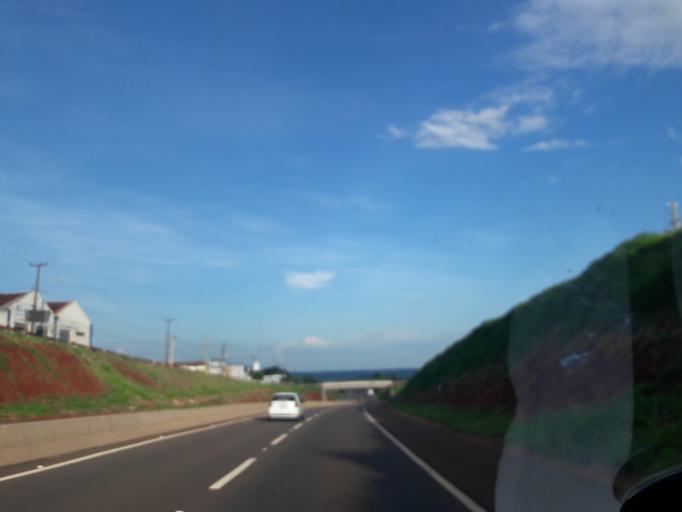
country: BR
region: Parana
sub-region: Engenheiro Beltrao
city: Engenheiro Beltrao
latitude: -23.8042
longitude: -52.2574
